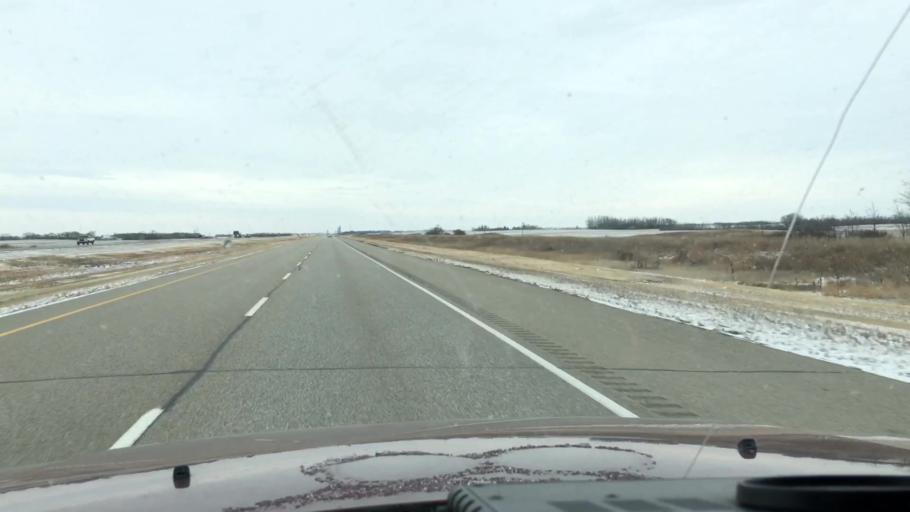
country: CA
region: Saskatchewan
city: Watrous
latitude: 51.3230
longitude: -106.0707
